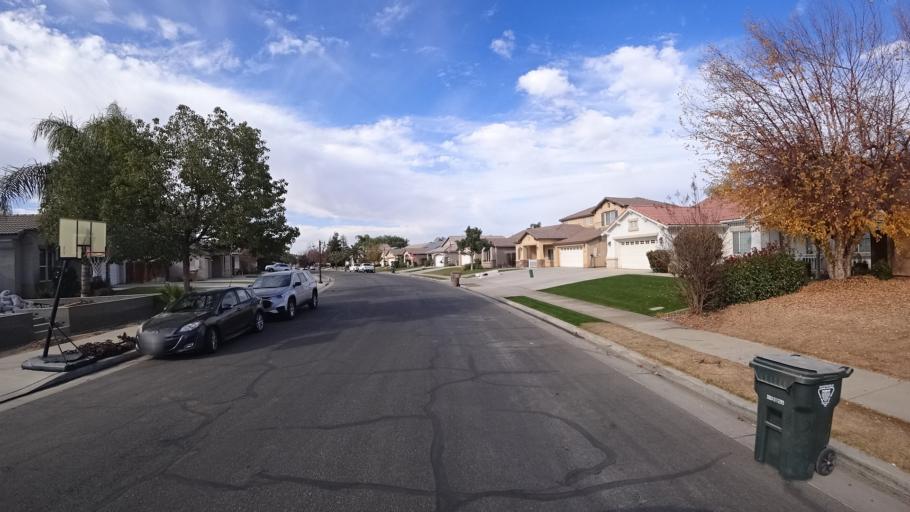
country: US
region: California
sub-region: Kern County
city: Greenacres
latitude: 35.4144
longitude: -119.1137
